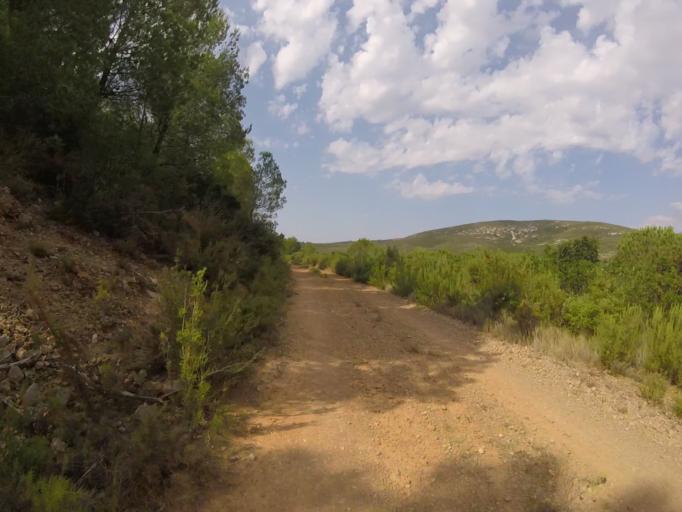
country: ES
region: Valencia
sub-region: Provincia de Castello
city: Alcala de Xivert
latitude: 40.3525
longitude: 0.2001
